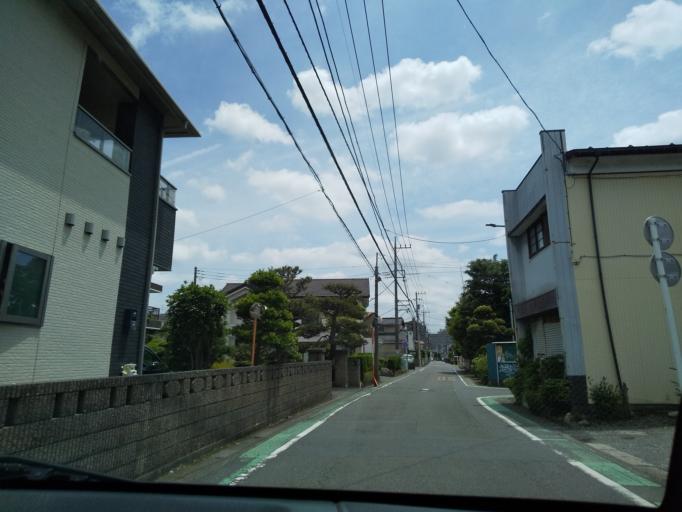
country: JP
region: Kanagawa
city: Zama
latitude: 35.5620
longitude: 139.3542
